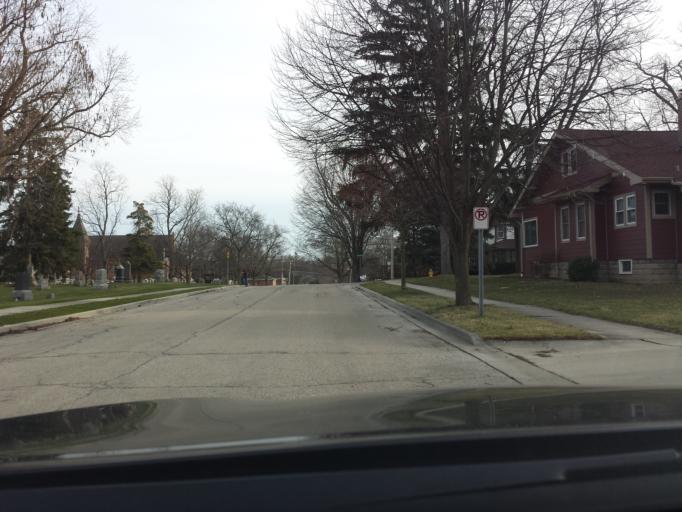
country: US
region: Illinois
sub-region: DuPage County
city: West Chicago
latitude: 41.8886
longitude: -88.2003
